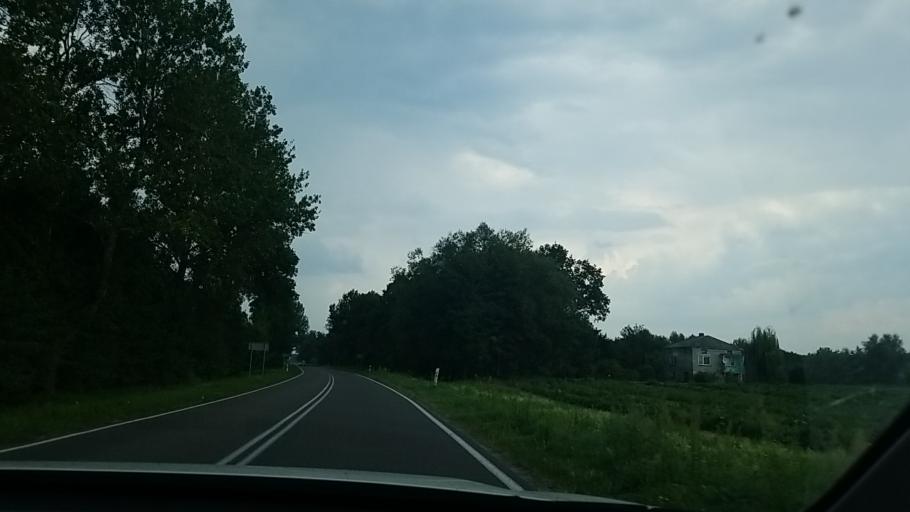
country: PL
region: Lublin Voivodeship
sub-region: Powiat leczynski
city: Cycow
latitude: 51.2434
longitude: 23.0899
